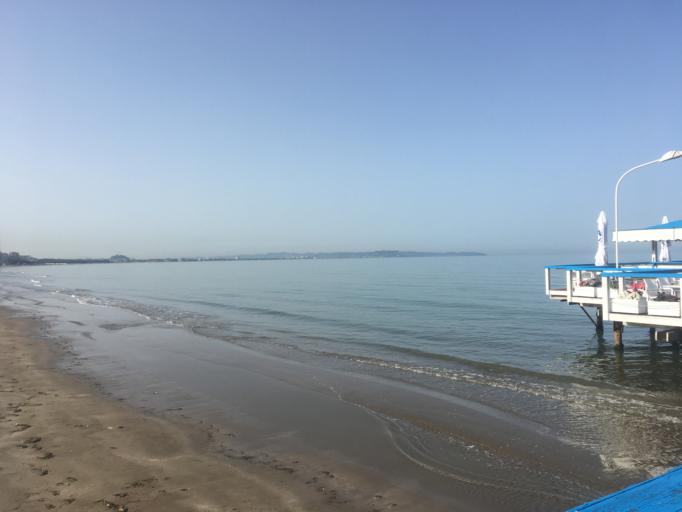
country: AL
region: Tirane
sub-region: Rrethi i Kavajes
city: Golem
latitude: 41.2803
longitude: 19.5122
